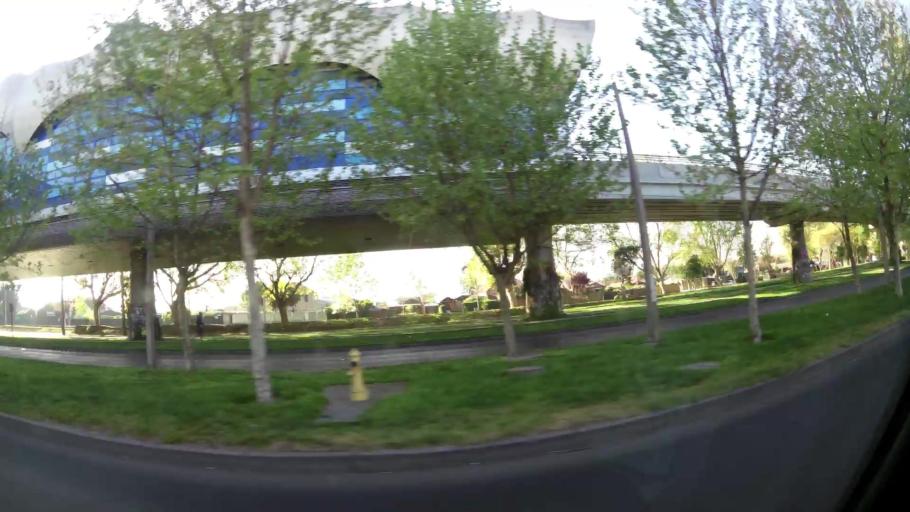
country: CL
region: Santiago Metropolitan
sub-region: Provincia de Santiago
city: Lo Prado
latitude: -33.4825
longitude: -70.7459
